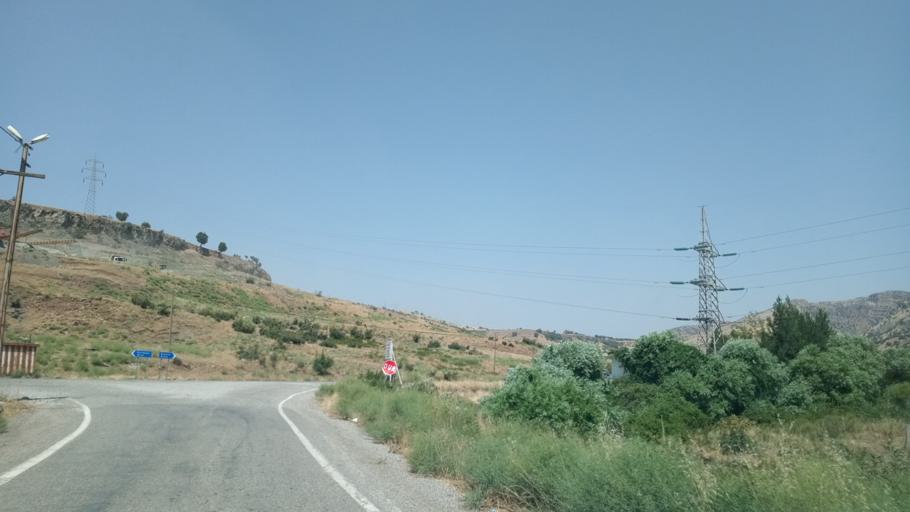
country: TR
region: Siirt
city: Dilektepe
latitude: 38.0607
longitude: 41.7792
